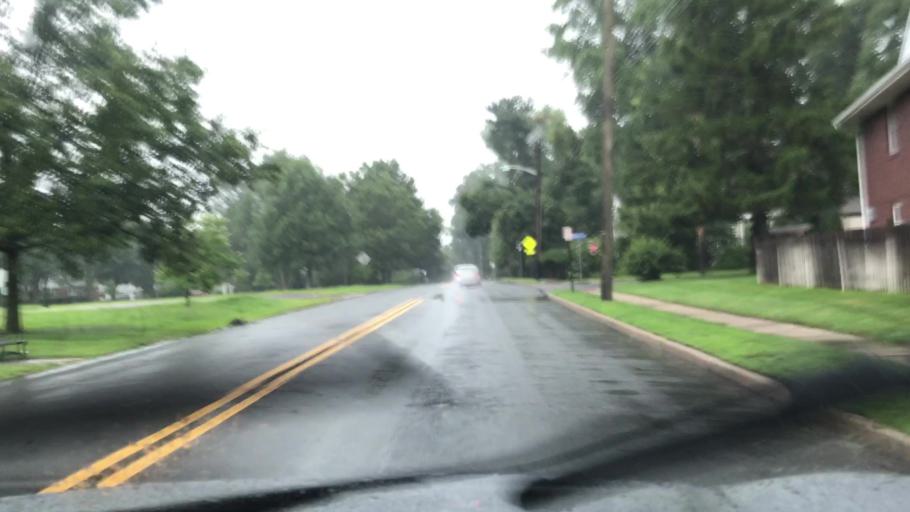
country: US
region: New Jersey
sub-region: Bergen County
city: Teaneck
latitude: 40.9127
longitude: -74.0247
